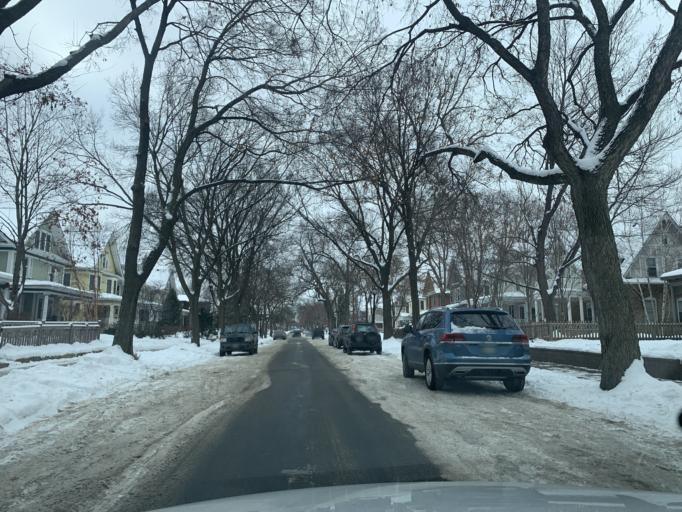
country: US
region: Minnesota
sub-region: Hennepin County
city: Minneapolis
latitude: 44.9621
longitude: -93.2957
